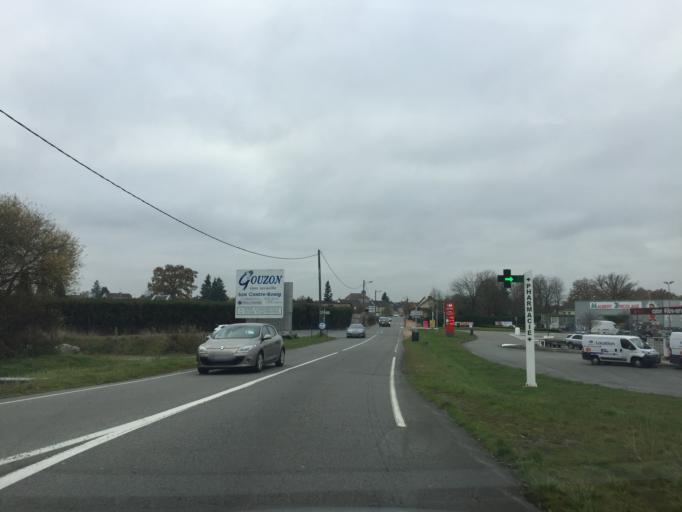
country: FR
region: Limousin
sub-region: Departement de la Creuse
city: Gouzon
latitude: 46.1976
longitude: 2.2389
